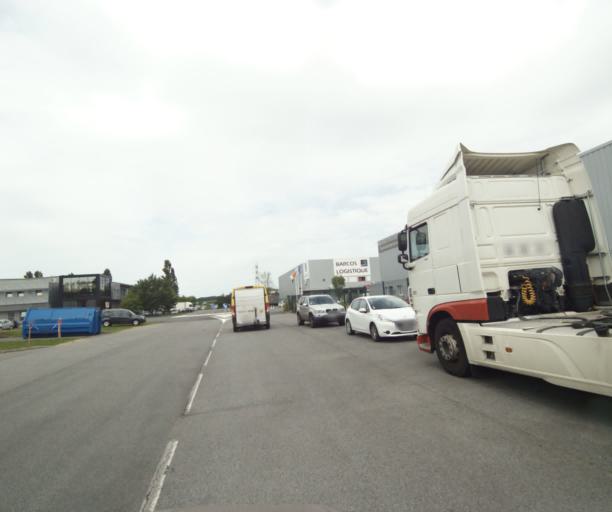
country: FR
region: Aquitaine
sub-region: Departement des Pyrenees-Atlantiques
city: Mouguerre
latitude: 43.4876
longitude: -1.4246
